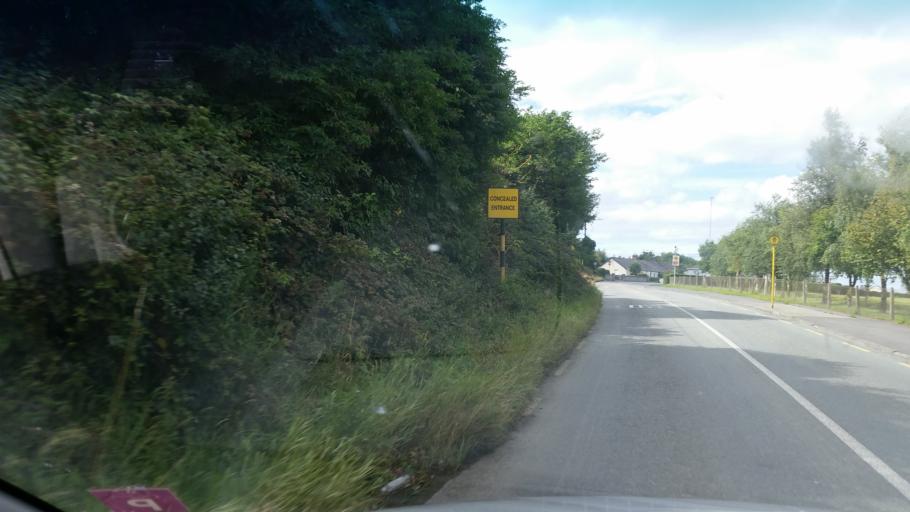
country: IE
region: Leinster
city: Kinsealy-Drinan
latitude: 53.4352
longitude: -6.1838
